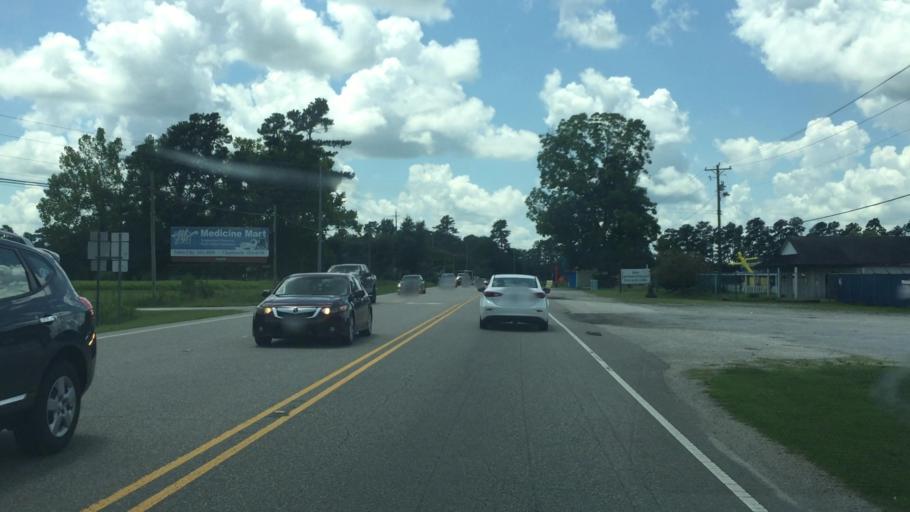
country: US
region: North Carolina
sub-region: Columbus County
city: Tabor City
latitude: 34.1608
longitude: -78.8469
